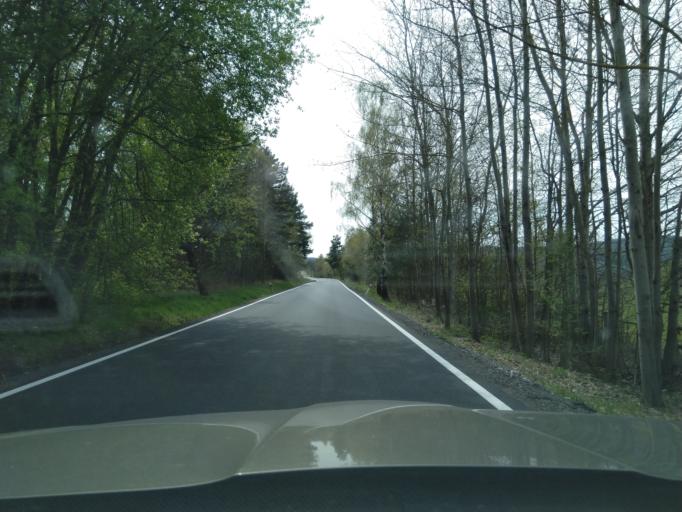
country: CZ
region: Jihocesky
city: Vacov
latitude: 49.1293
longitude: 13.7397
